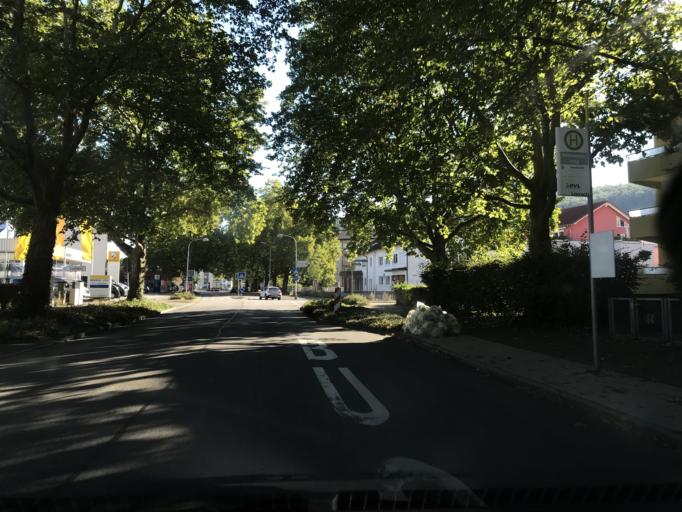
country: DE
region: Baden-Wuerttemberg
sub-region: Freiburg Region
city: Loerrach
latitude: 47.6209
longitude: 7.6731
